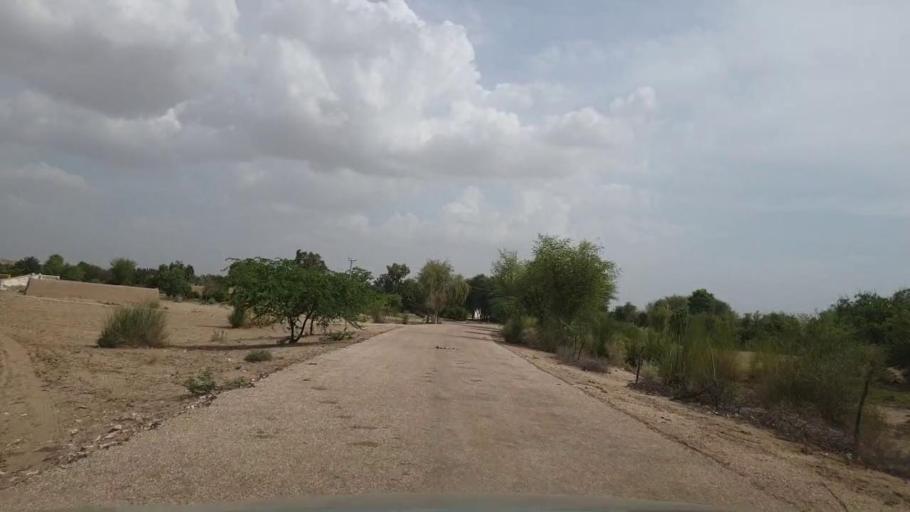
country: PK
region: Sindh
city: Bozdar
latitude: 27.0848
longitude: 69.0139
